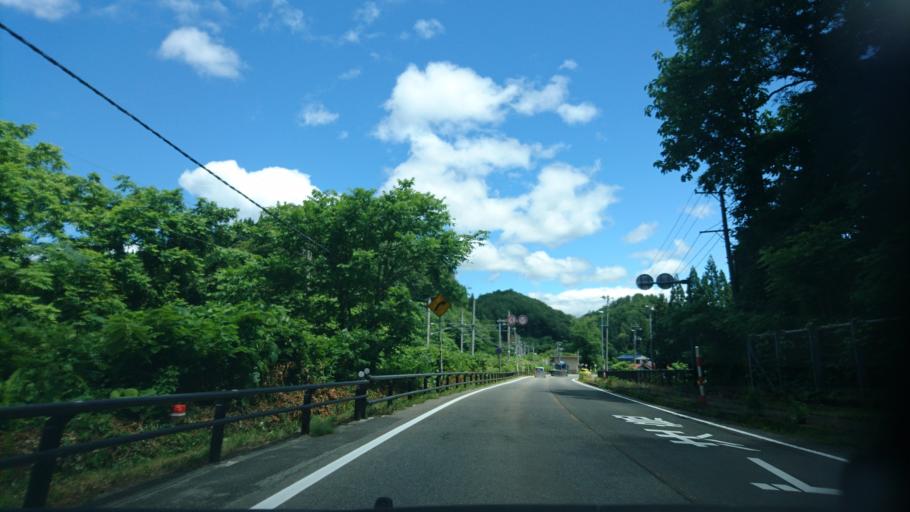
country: JP
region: Akita
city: Kakunodatemachi
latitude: 39.6803
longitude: 140.7035
